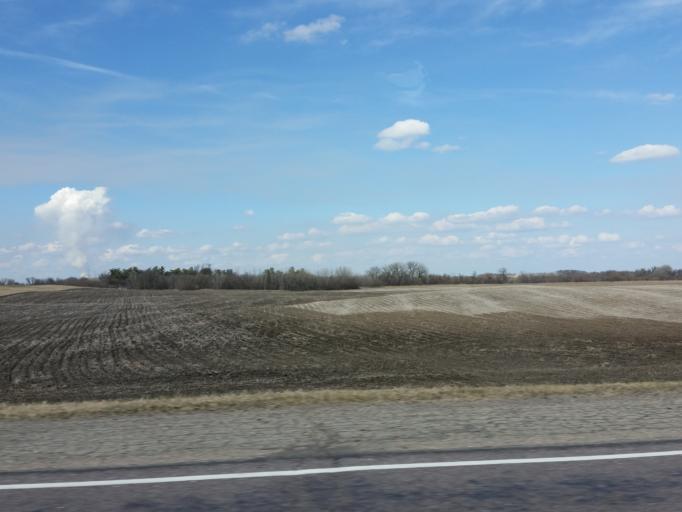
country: US
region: Minnesota
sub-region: Lac qui Parle County
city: Madison
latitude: 44.9358
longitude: -96.3477
